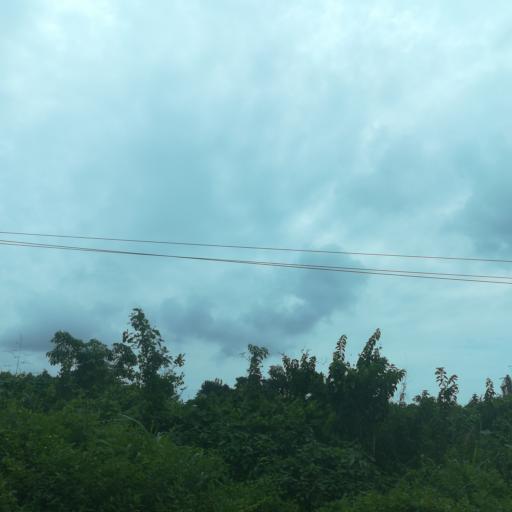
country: NG
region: Ogun
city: Odogbolu
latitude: 6.6700
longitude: 3.7107
